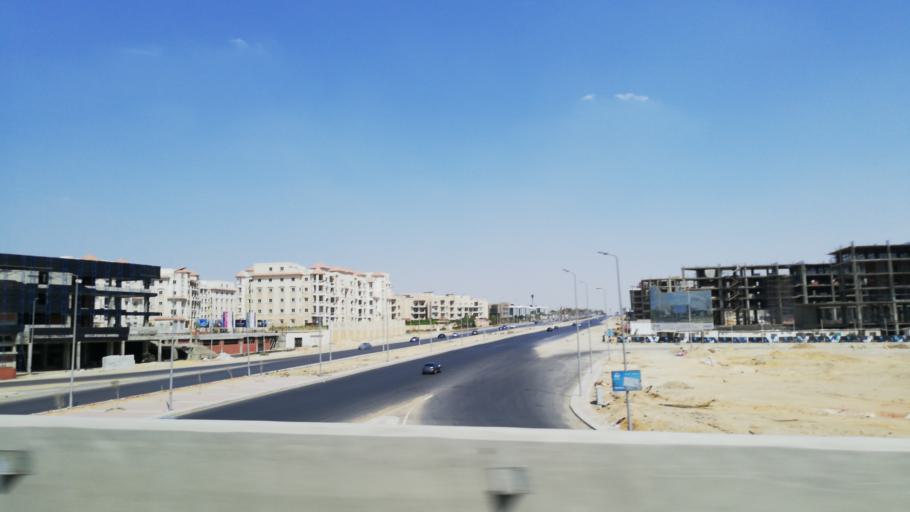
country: EG
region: Muhafazat al Qalyubiyah
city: Al Khankah
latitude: 30.0285
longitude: 31.4750
